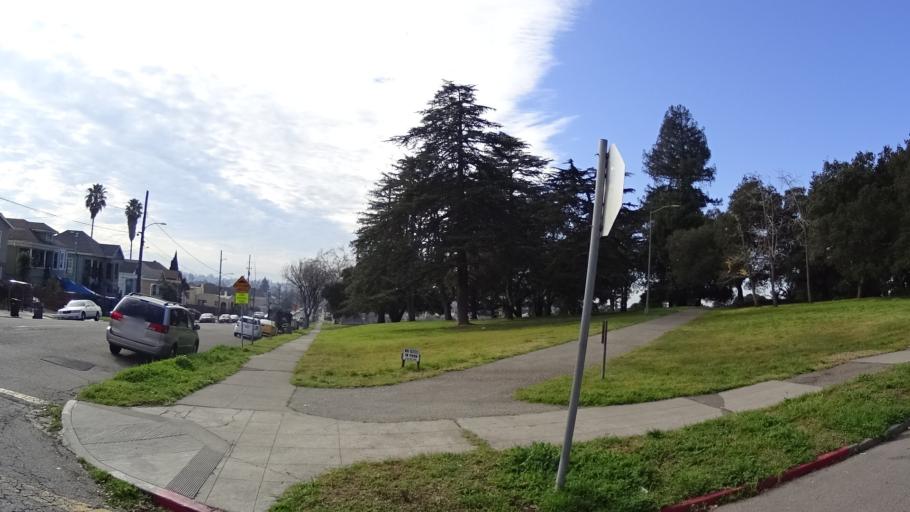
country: US
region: California
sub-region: Alameda County
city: Alameda
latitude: 37.7905
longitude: -122.2391
